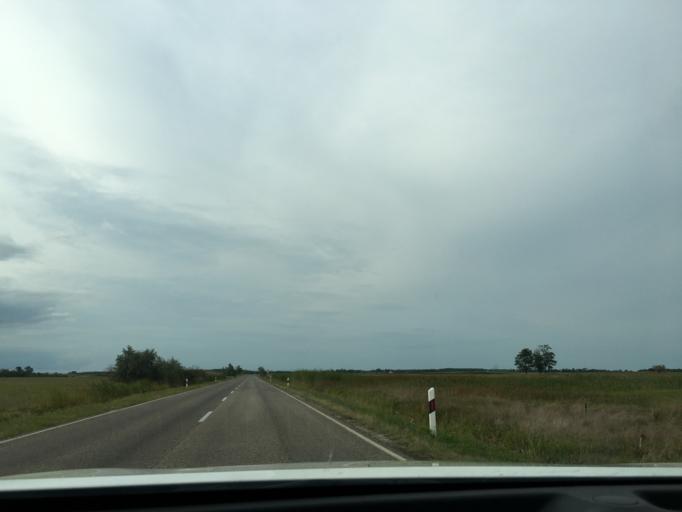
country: HU
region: Hajdu-Bihar
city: Egyek
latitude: 47.5713
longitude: 20.8595
